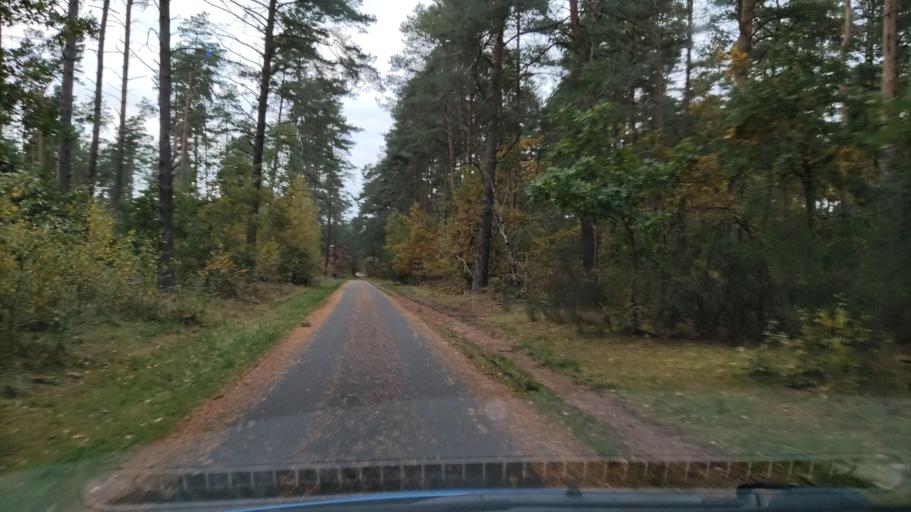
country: DE
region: Lower Saxony
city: Karwitz
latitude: 53.1301
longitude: 10.9901
